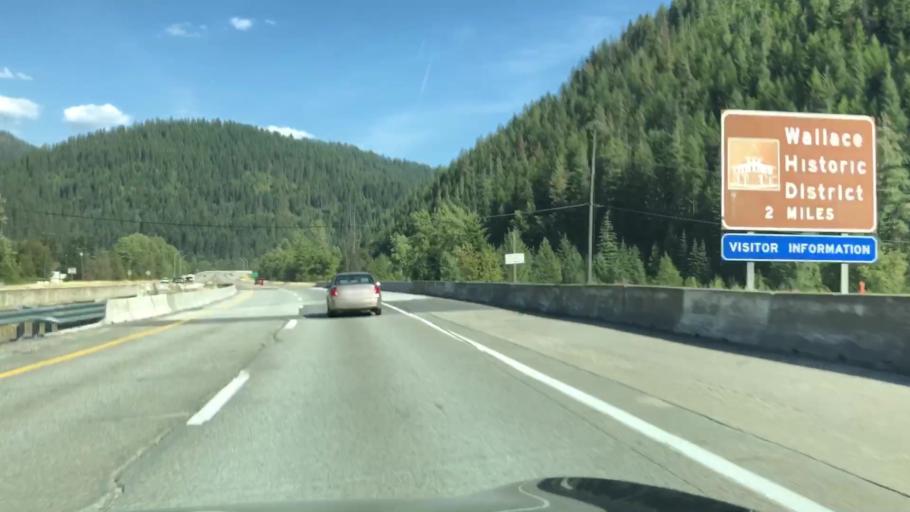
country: US
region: Idaho
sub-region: Shoshone County
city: Osburn
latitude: 47.4910
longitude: -115.9671
